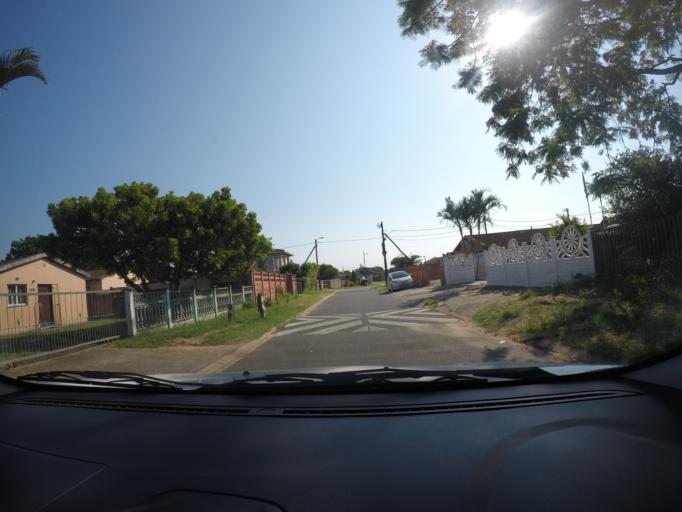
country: ZA
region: KwaZulu-Natal
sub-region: uThungulu District Municipality
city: Richards Bay
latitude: -28.7162
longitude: 32.0422
